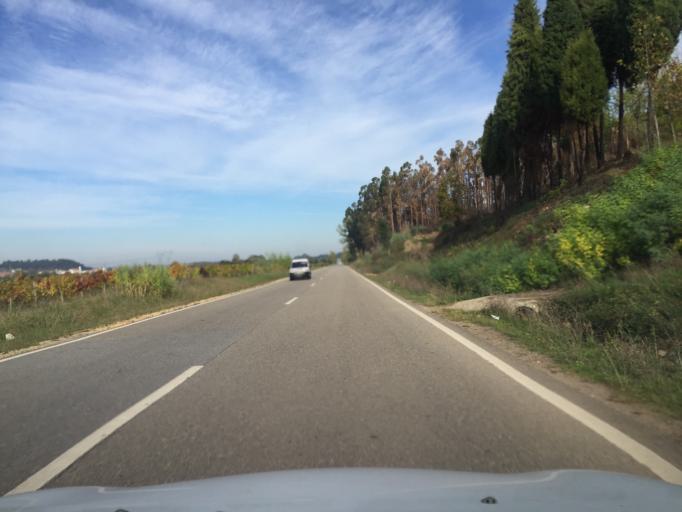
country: PT
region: Aveiro
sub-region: Anadia
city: Anadia
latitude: 40.4304
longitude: -8.4154
